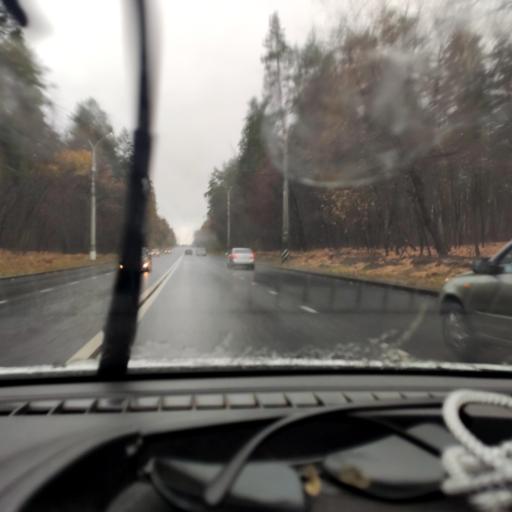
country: RU
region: Samara
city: Zhigulevsk
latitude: 53.4983
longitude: 49.4632
